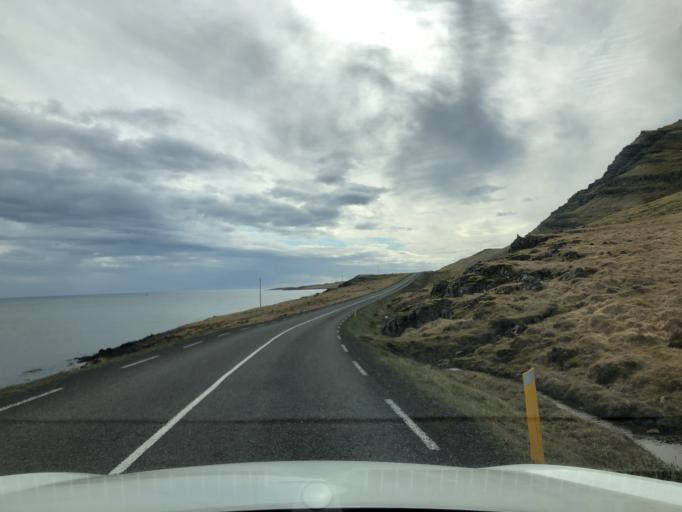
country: IS
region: East
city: Eskifjoerdur
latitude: 64.8228
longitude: -13.9075
